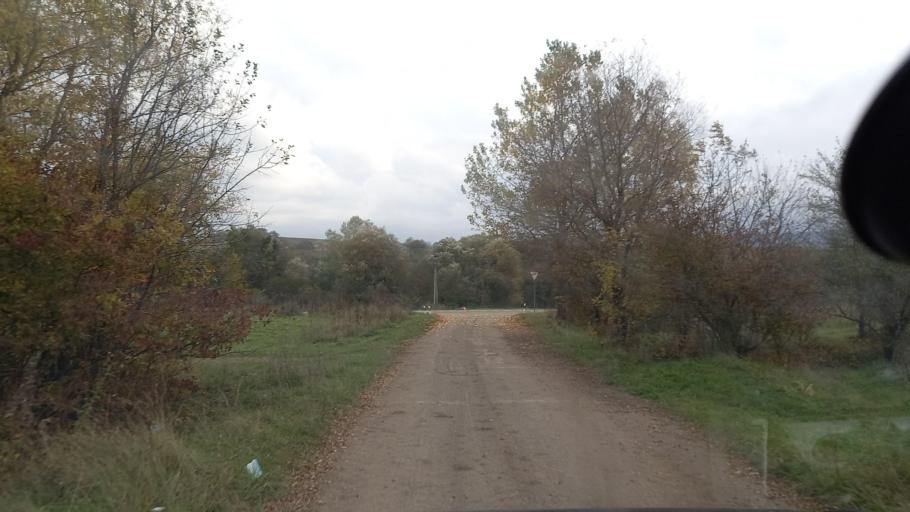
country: RU
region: Krasnodarskiy
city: Gubskaya
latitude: 44.3022
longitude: 40.5531
